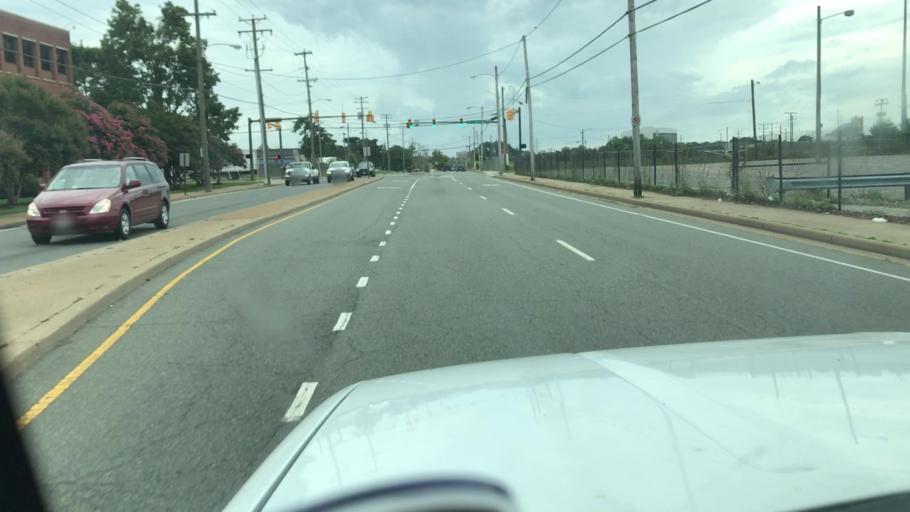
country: US
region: Virginia
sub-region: City of Richmond
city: Richmond
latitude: 37.5710
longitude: -77.4609
